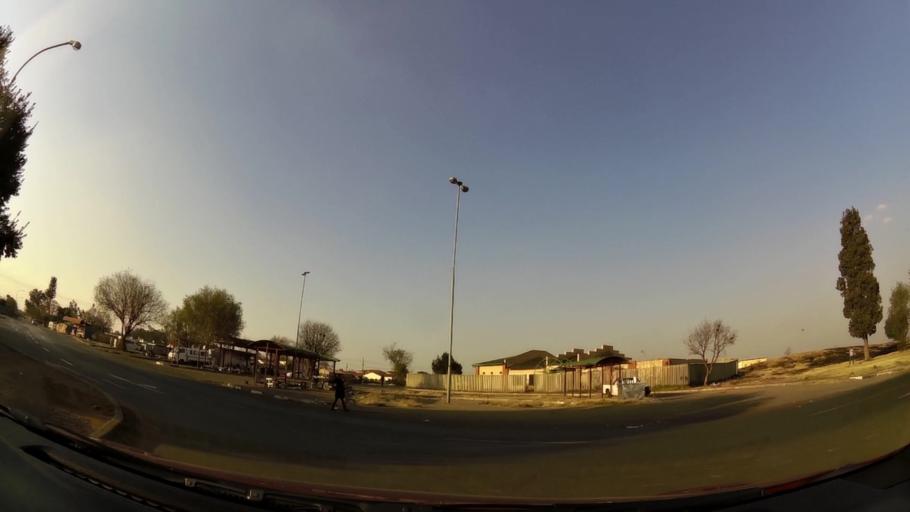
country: ZA
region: Gauteng
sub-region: City of Johannesburg Metropolitan Municipality
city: Soweto
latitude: -26.2924
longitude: 27.8954
